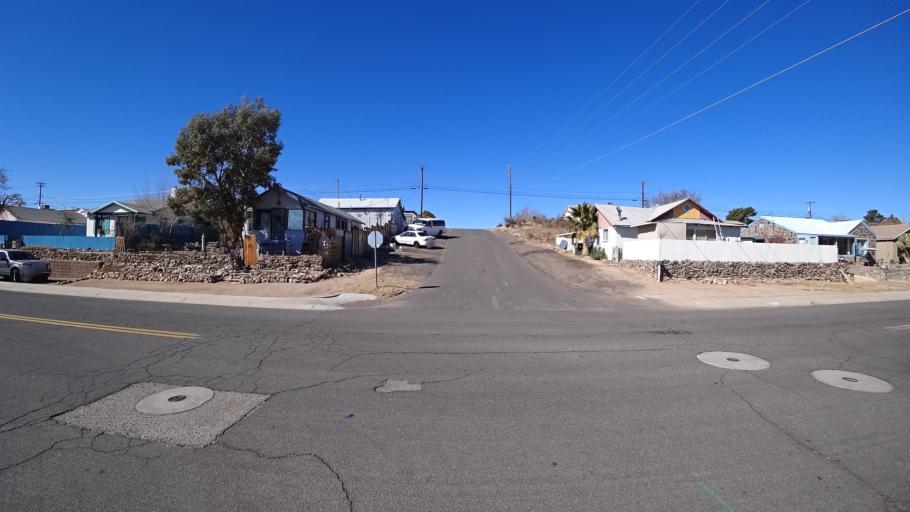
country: US
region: Arizona
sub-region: Mohave County
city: Kingman
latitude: 35.1946
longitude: -114.0613
